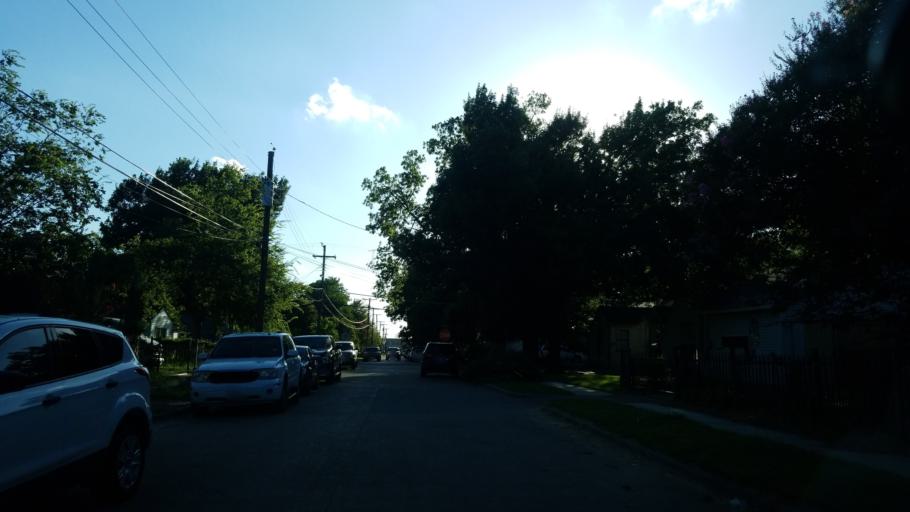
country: US
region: Texas
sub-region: Dallas County
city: Balch Springs
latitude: 32.7737
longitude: -96.6957
